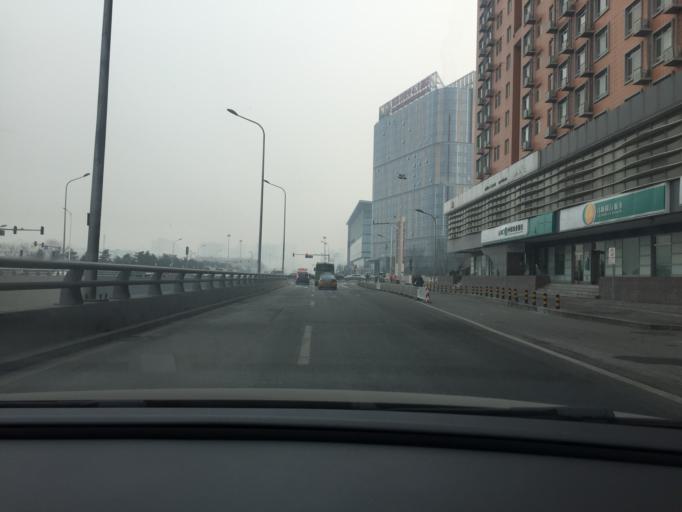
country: CN
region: Beijing
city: Datun
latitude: 40.0005
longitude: 116.3792
